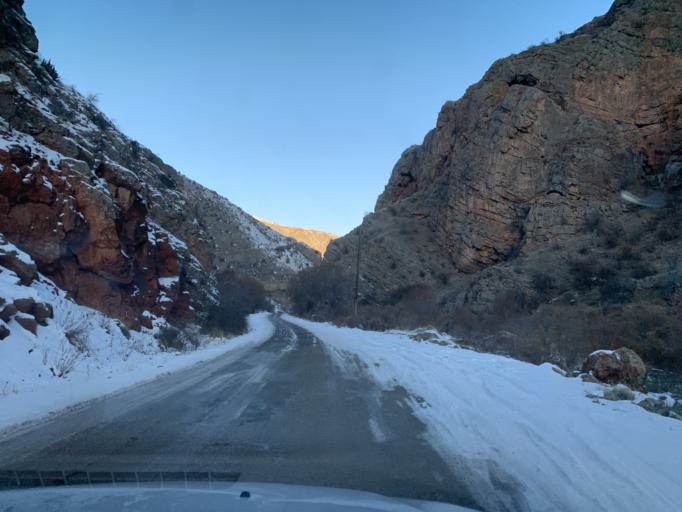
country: AM
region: Vayots' Dzori Marz
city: Areni
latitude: 39.6870
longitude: 45.2237
